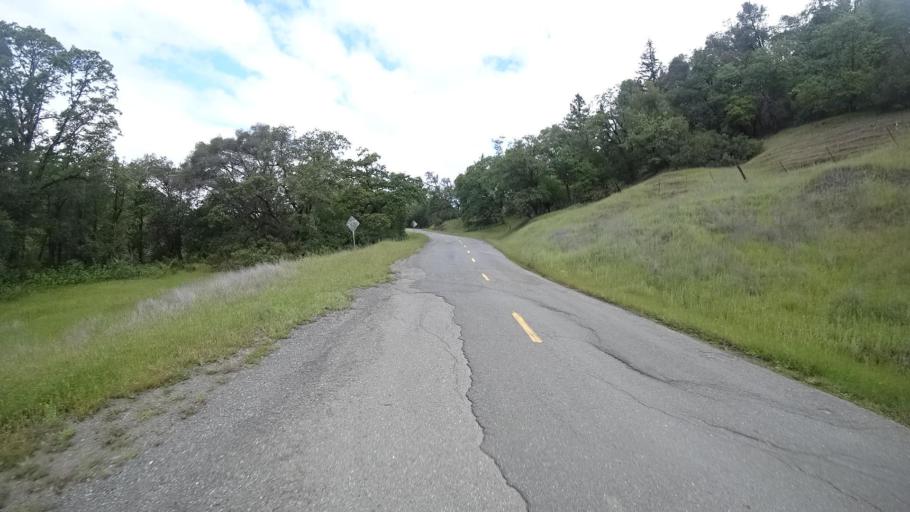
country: US
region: California
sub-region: Humboldt County
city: Redway
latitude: 40.1751
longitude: -123.5994
